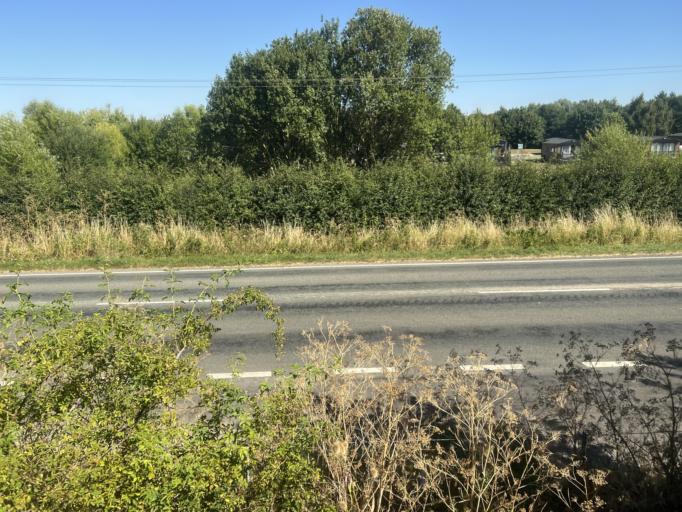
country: GB
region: England
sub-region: Lincolnshire
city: Kirton
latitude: 52.9760
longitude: -0.1204
